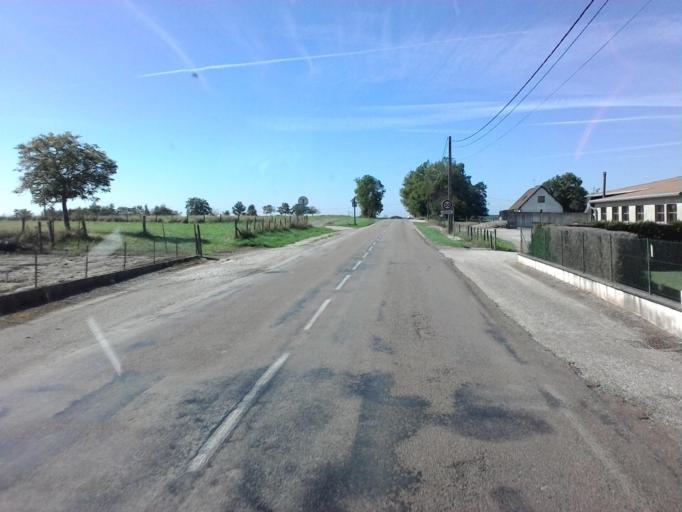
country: FR
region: Bourgogne
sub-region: Departement de l'Yonne
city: Tonnerre
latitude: 47.9691
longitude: 4.0413
